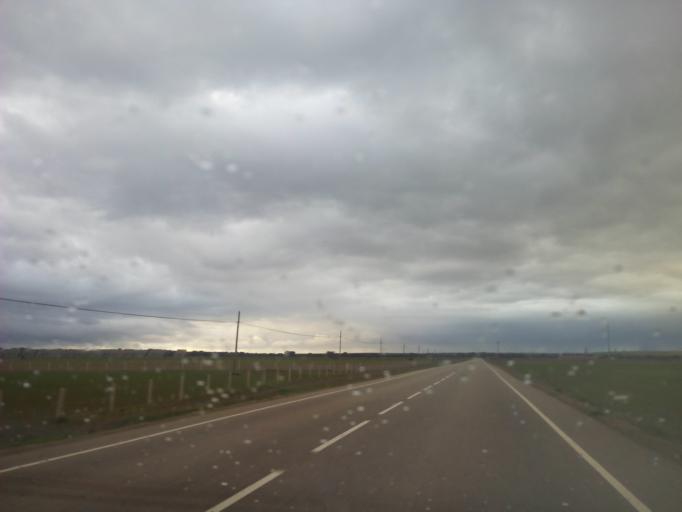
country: ES
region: Castille and Leon
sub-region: Provincia de Salamanca
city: Abusejo
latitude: 40.7146
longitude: -6.1452
